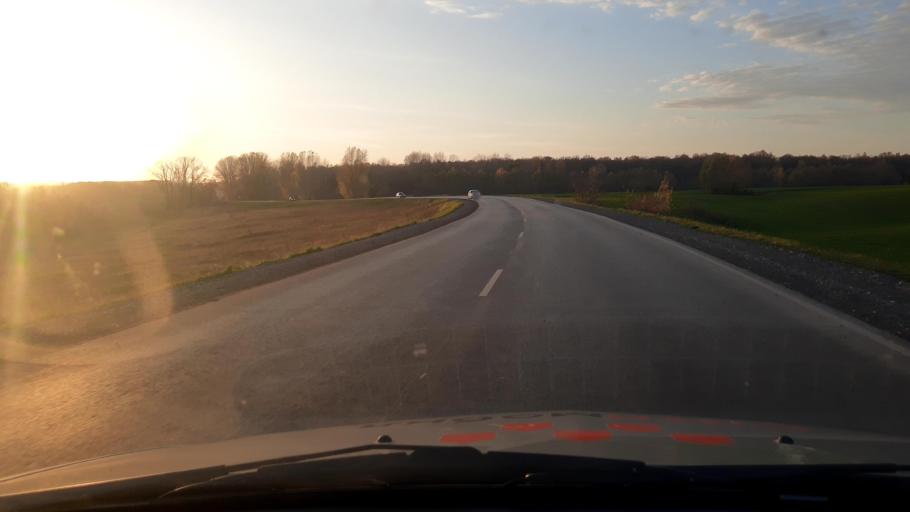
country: RU
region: Bashkortostan
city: Mikhaylovka
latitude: 54.8333
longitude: 55.9402
